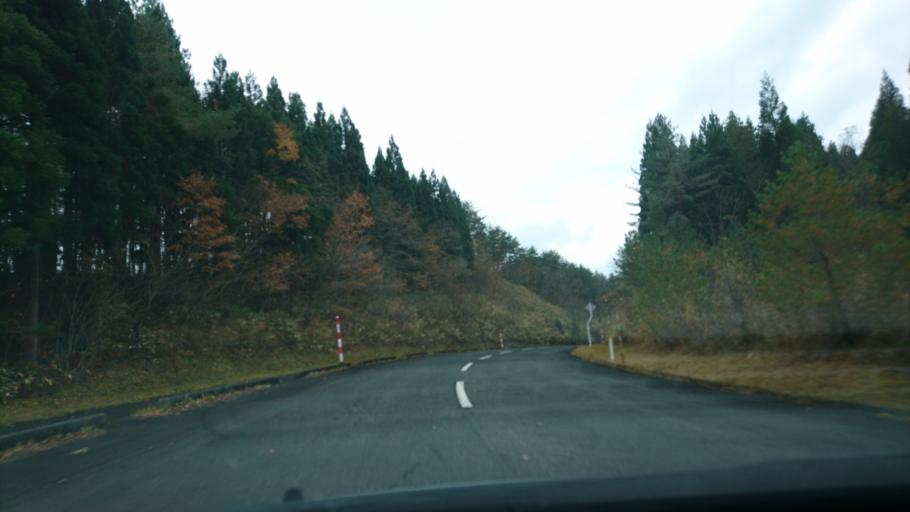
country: JP
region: Iwate
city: Ichinoseki
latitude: 38.9230
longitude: 140.9137
